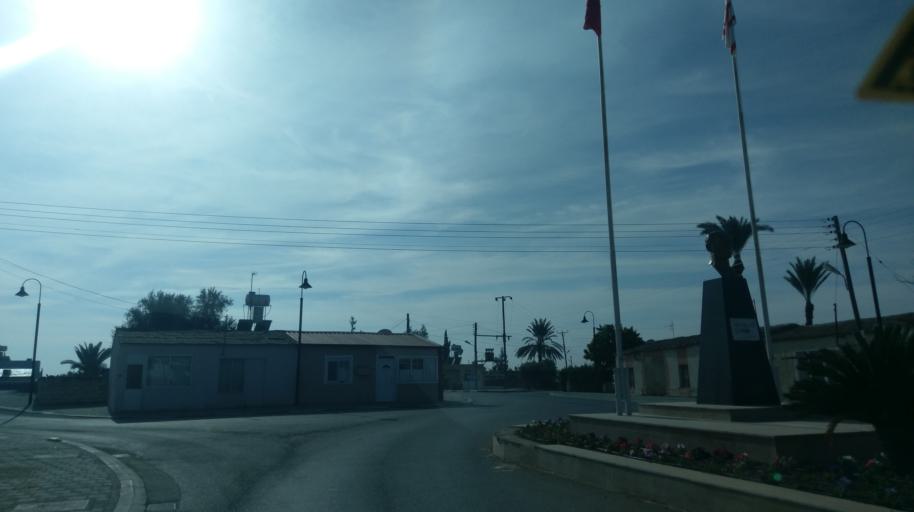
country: CY
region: Lefkosia
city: Geri
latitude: 35.2264
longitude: 33.5135
